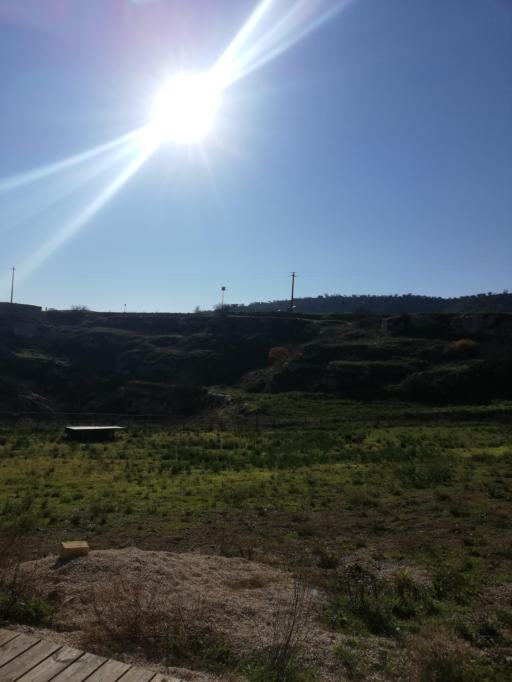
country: IT
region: Apulia
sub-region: Provincia di Bari
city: Gravina in Puglia
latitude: 40.8220
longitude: 16.4124
